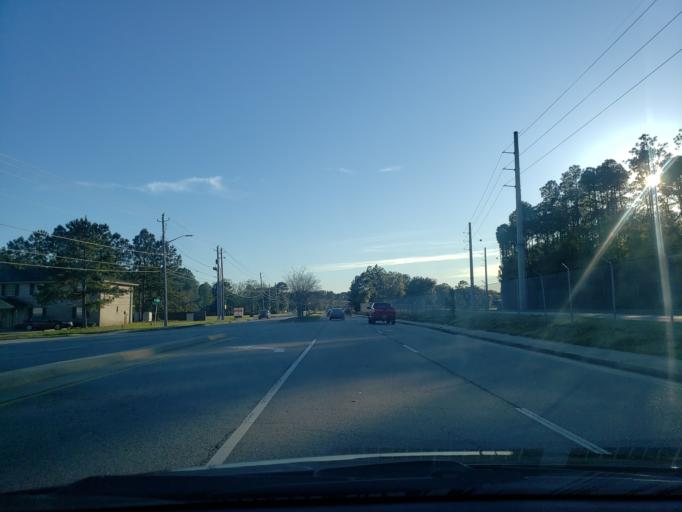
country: US
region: Georgia
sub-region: Chatham County
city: Montgomery
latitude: 32.0011
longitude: -81.1447
